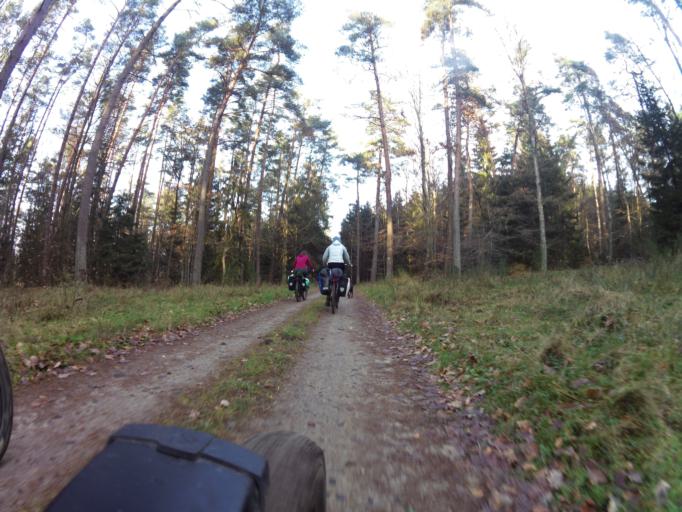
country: PL
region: West Pomeranian Voivodeship
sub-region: Powiat koszalinski
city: Polanow
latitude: 54.0889
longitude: 16.6467
